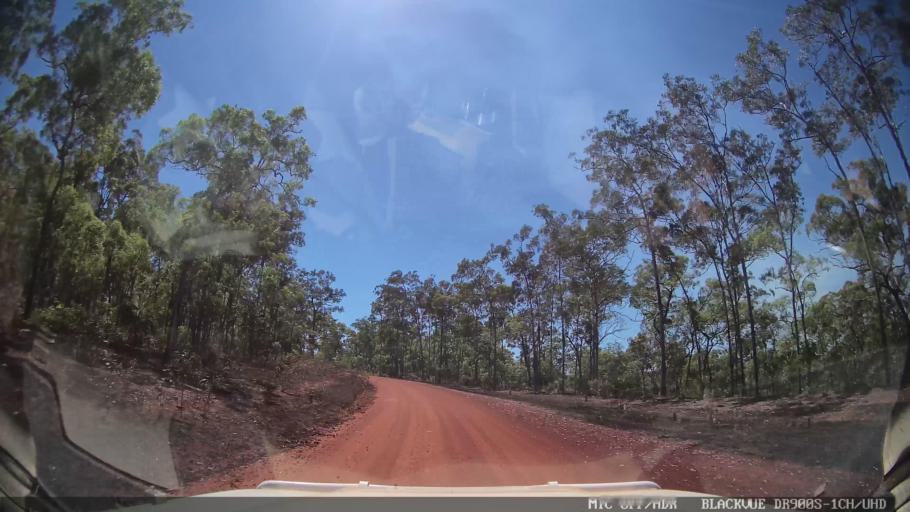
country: AU
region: Queensland
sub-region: Torres
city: Thursday Island
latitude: -10.9740
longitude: 142.3395
